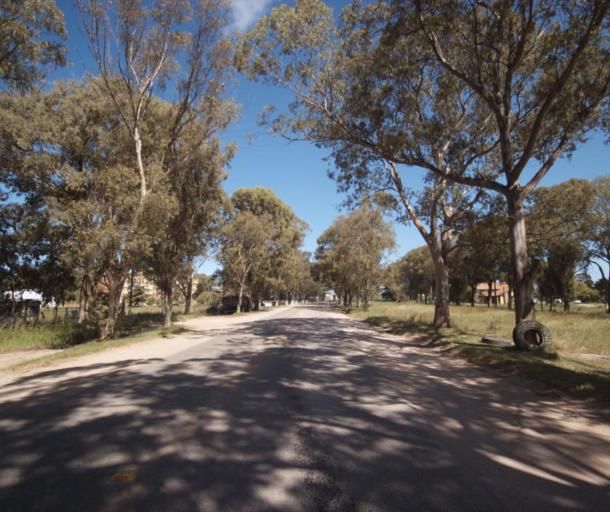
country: BR
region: Rio Grande do Sul
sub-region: Chui
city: Chui
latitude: -33.6869
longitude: -53.4479
